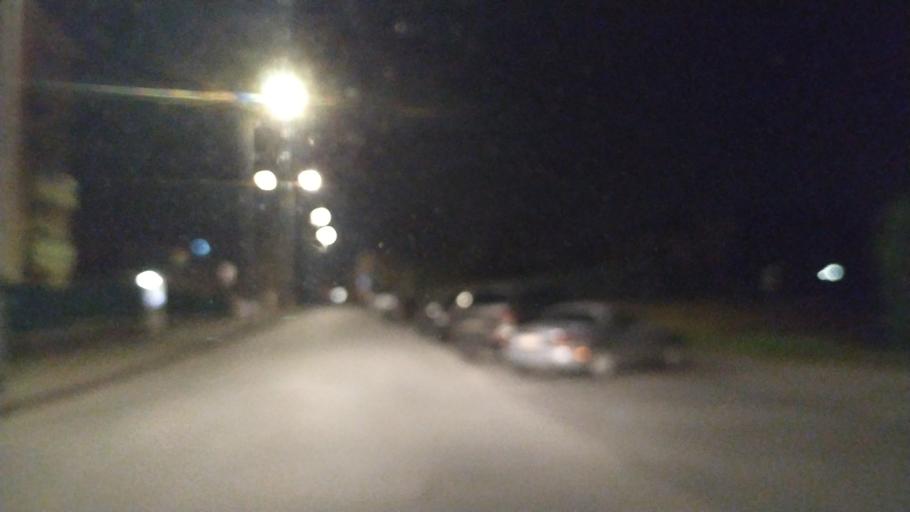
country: IT
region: Piedmont
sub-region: Provincia di Biella
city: Ponderano
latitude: 45.5510
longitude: 8.0625
